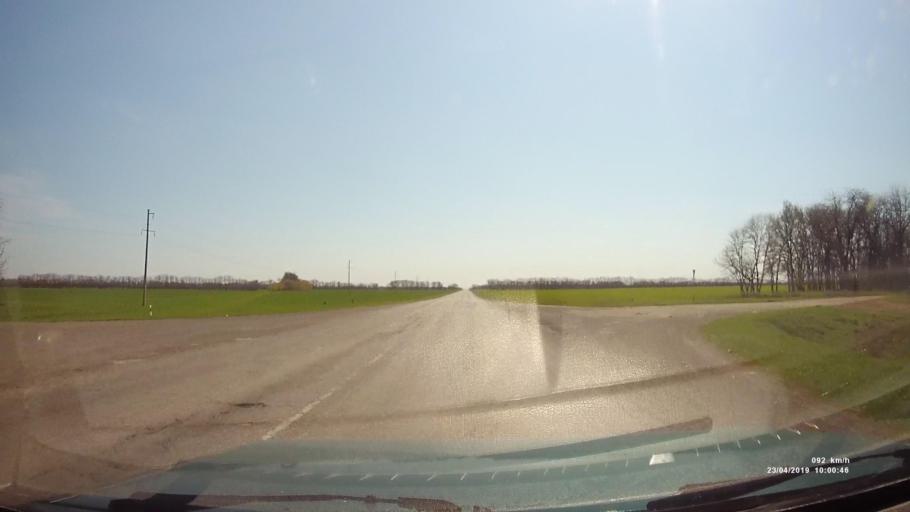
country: RU
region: Rostov
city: Sovetskoye
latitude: 46.7688
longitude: 42.1379
